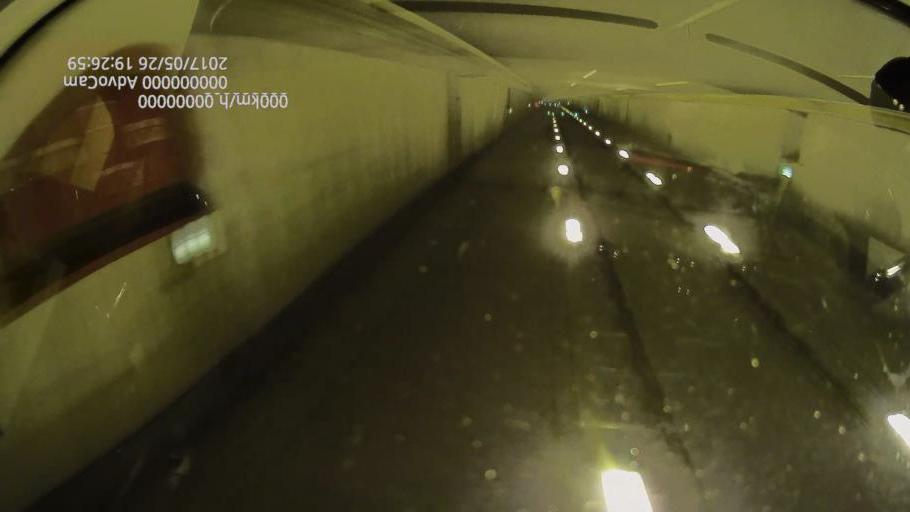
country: GR
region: Central Macedonia
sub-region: Nomos Thessalonikis
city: Nea Malgara
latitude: 40.5924
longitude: 22.6618
